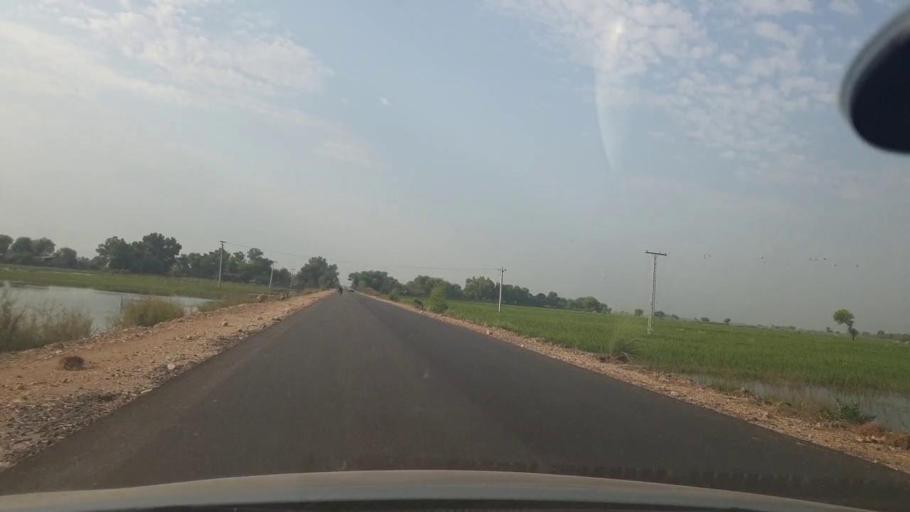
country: PK
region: Sindh
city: Jacobabad
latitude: 28.1141
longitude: 68.3269
